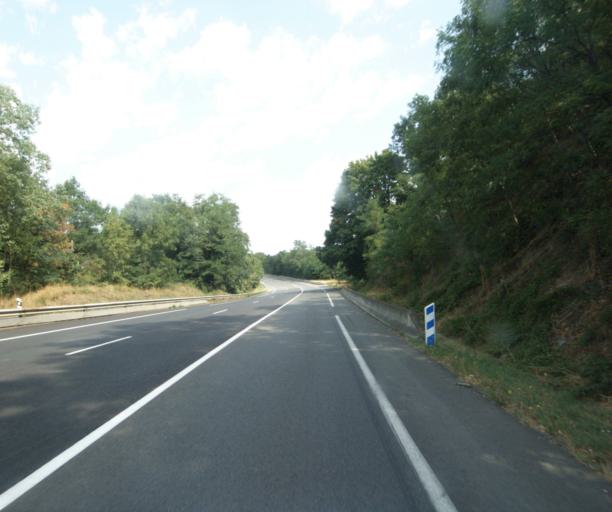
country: FR
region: Rhone-Alpes
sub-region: Departement du Rhone
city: Lentilly
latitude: 45.8300
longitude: 4.6639
